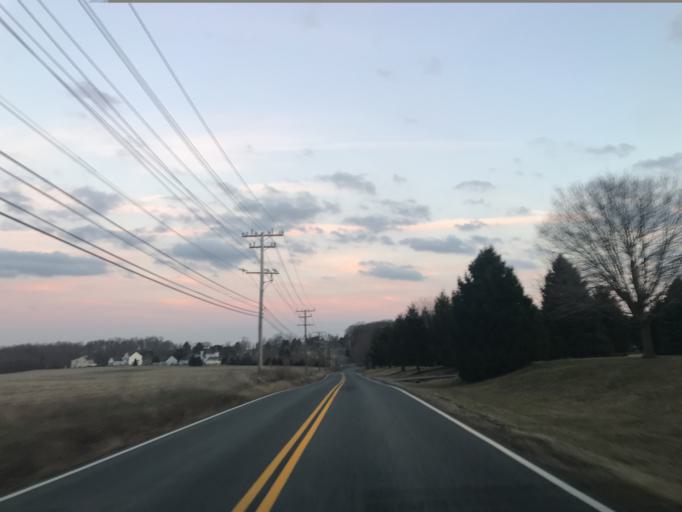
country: US
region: Maryland
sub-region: Harford County
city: Bel Air South
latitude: 39.5397
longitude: -76.2857
